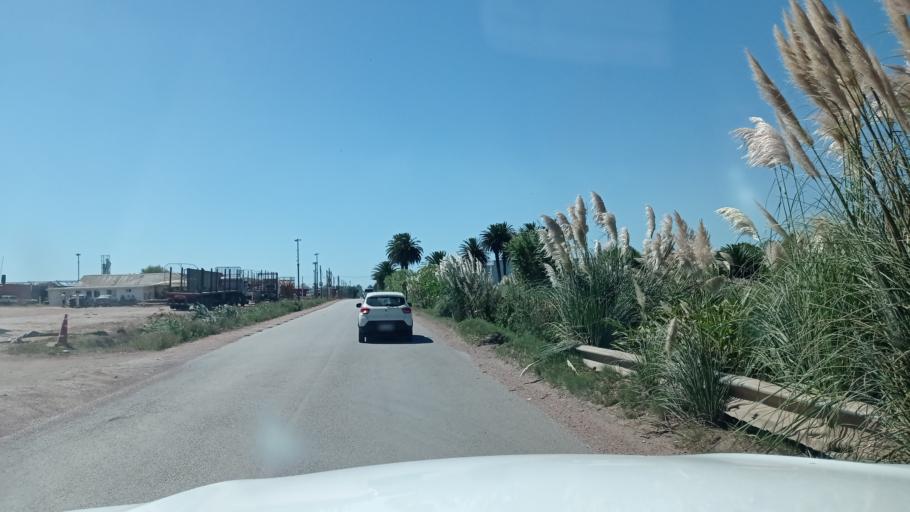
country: UY
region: Montevideo
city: Pajas Blancas
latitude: -34.8669
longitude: -56.2873
